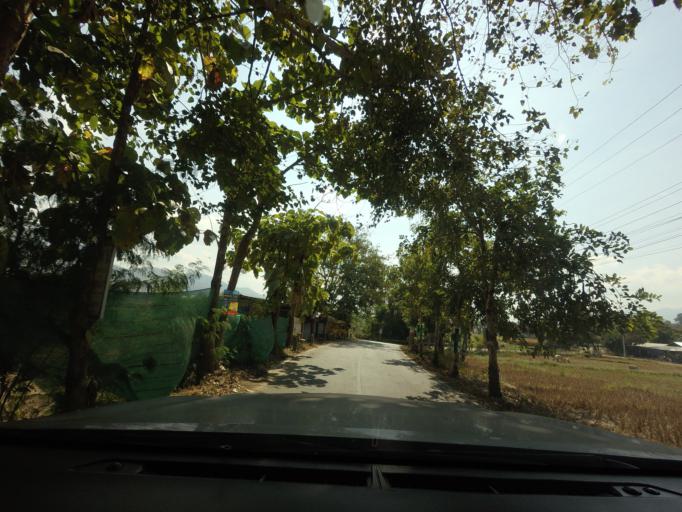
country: TH
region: Mae Hong Son
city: Wiang Nuea
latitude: 19.3907
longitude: 98.4429
